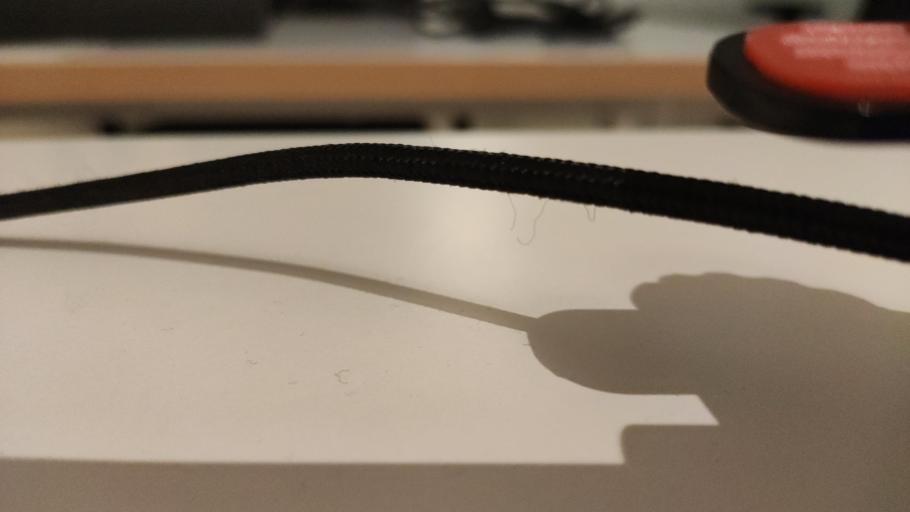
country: RU
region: Moskovskaya
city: Kurovskoye
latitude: 55.5819
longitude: 38.8896
